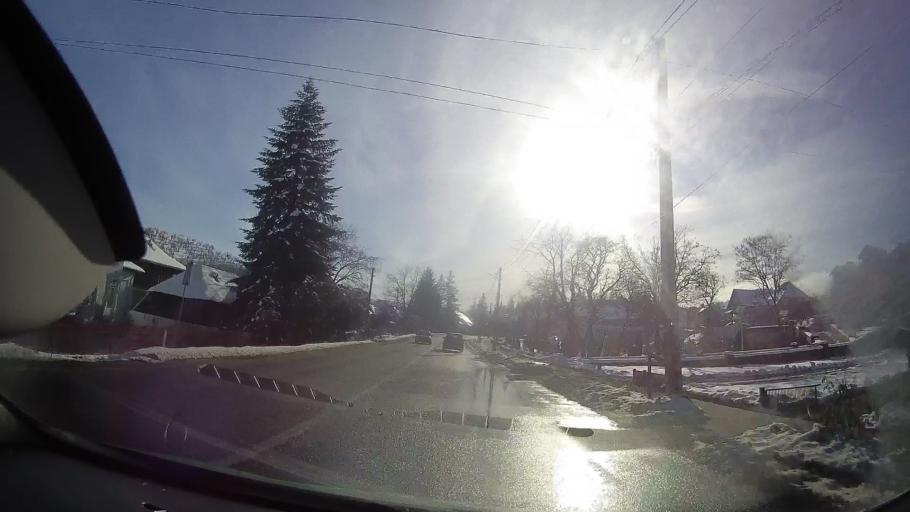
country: RO
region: Neamt
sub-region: Comuna Baltatesti
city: Baltatesti
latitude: 47.1231
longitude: 26.3100
